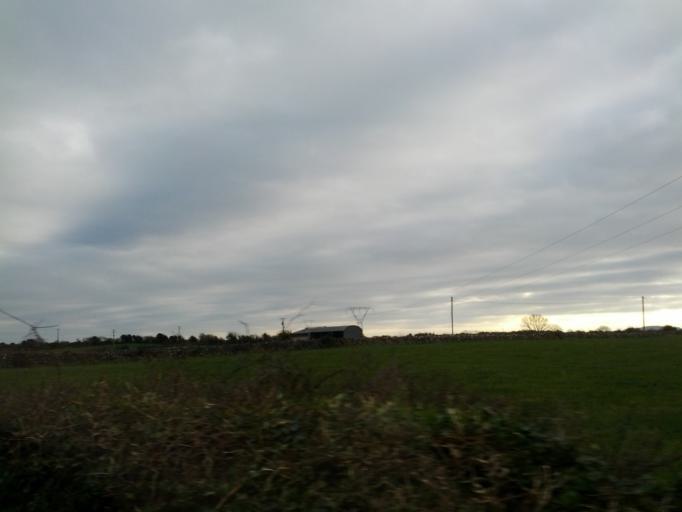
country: IE
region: Connaught
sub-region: County Galway
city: Oranmore
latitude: 53.1699
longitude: -8.8864
